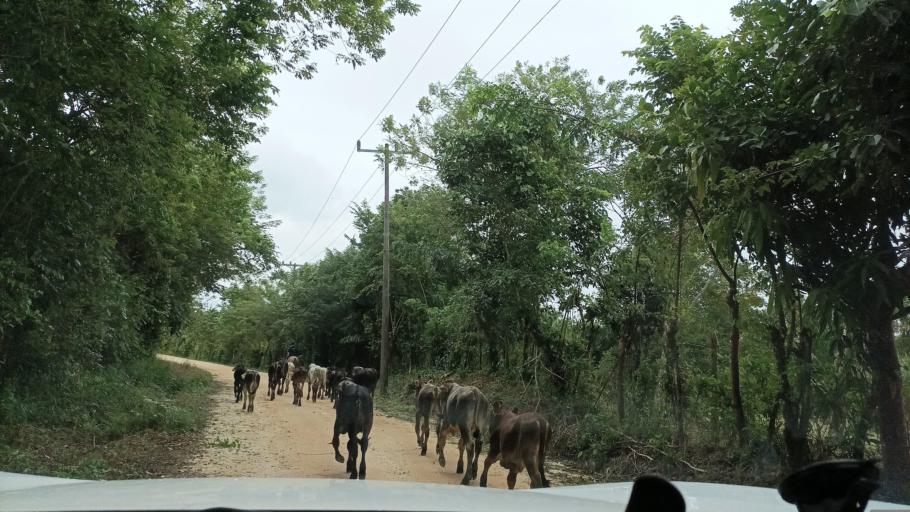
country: MX
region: Veracruz
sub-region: Moloacan
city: Cuichapa
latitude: 17.8190
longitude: -94.3540
